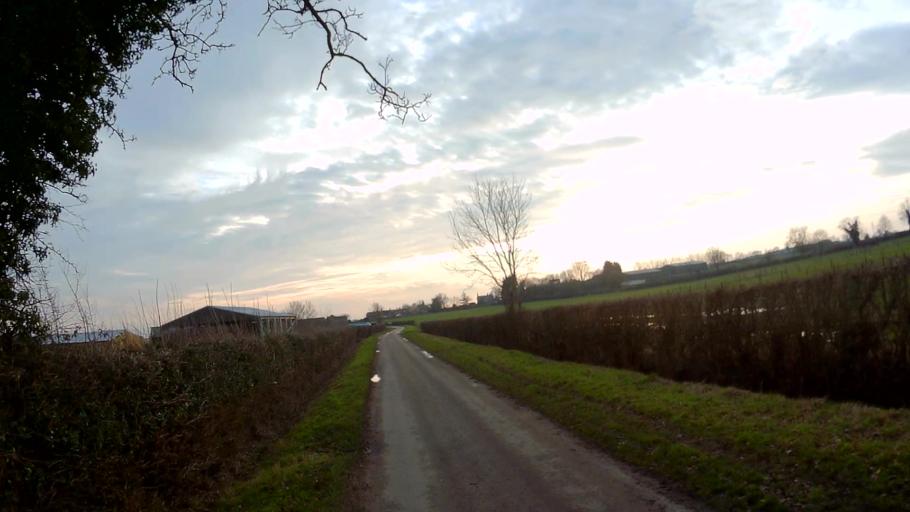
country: GB
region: England
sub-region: Lincolnshire
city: Bourne
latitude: 52.8163
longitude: -0.3983
